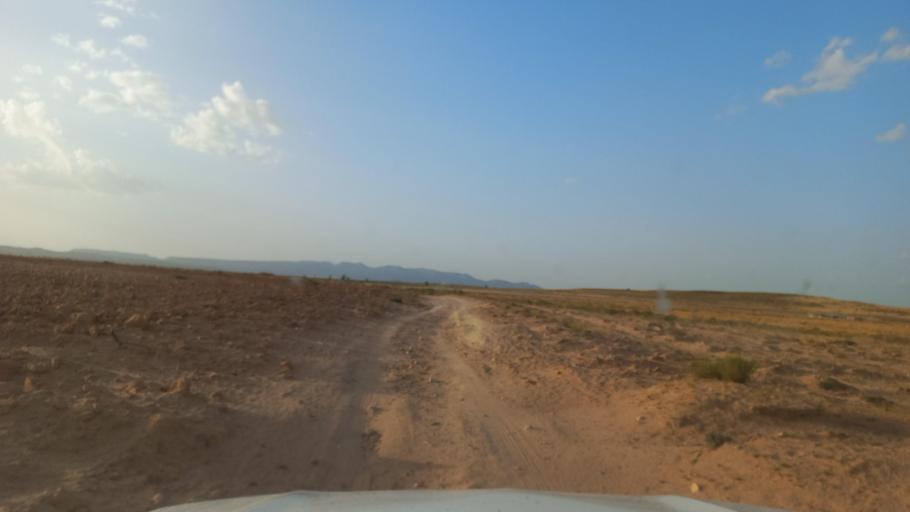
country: TN
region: Al Qasrayn
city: Sbiba
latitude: 35.3058
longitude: 9.0744
